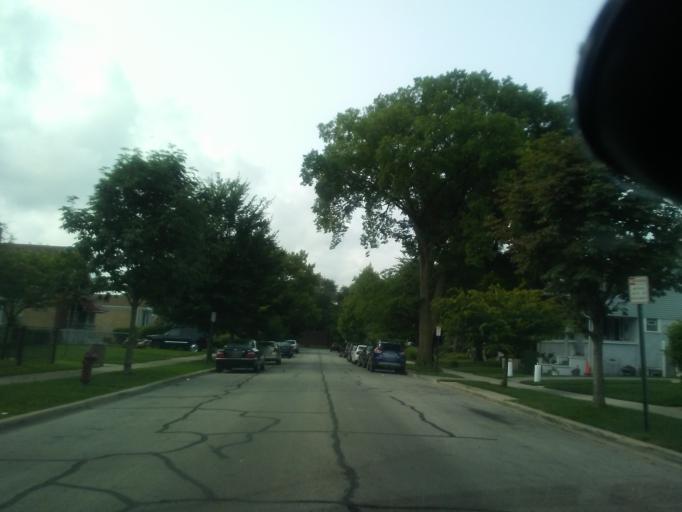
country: US
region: Illinois
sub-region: Cook County
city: Evanston
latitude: 42.0496
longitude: -87.7013
